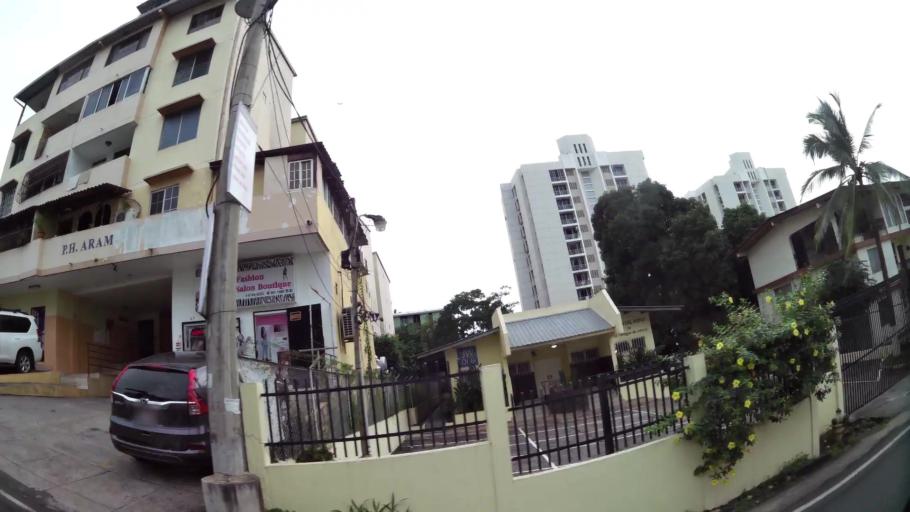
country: PA
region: Panama
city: Panama
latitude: 9.0001
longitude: -79.5141
